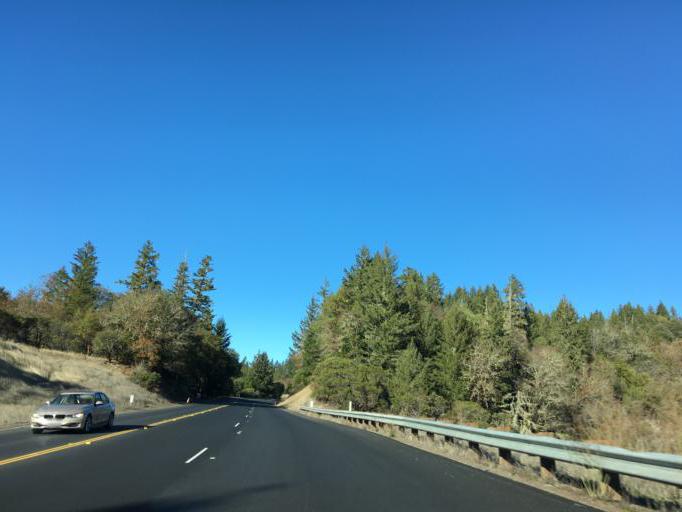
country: US
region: California
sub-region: Mendocino County
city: Laytonville
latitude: 39.7778
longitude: -123.5436
